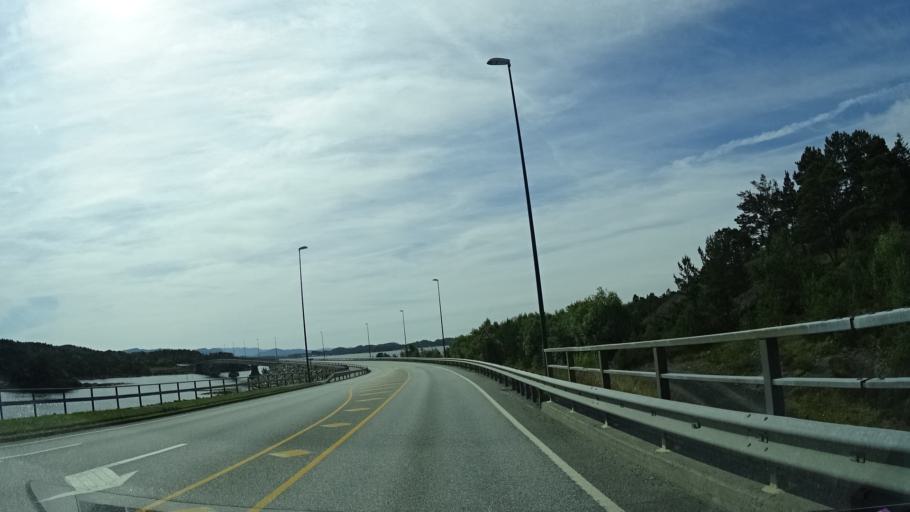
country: NO
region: Hordaland
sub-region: Bomlo
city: Mosterhamn
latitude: 59.7368
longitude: 5.3463
